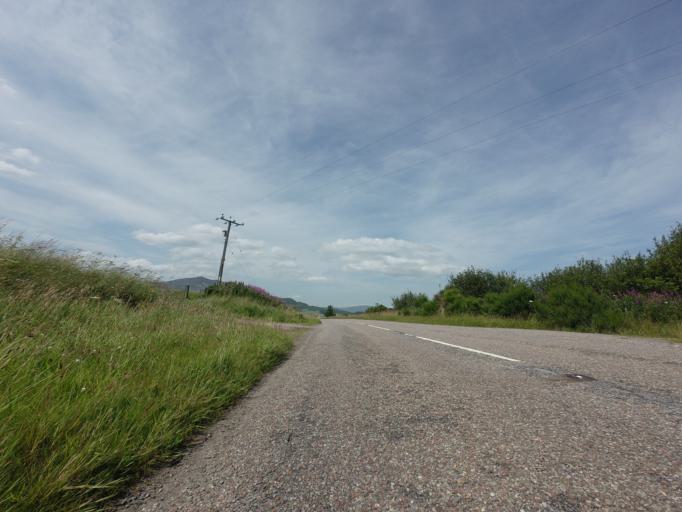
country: GB
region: Scotland
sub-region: Highland
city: Tain
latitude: 57.8374
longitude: -4.1848
